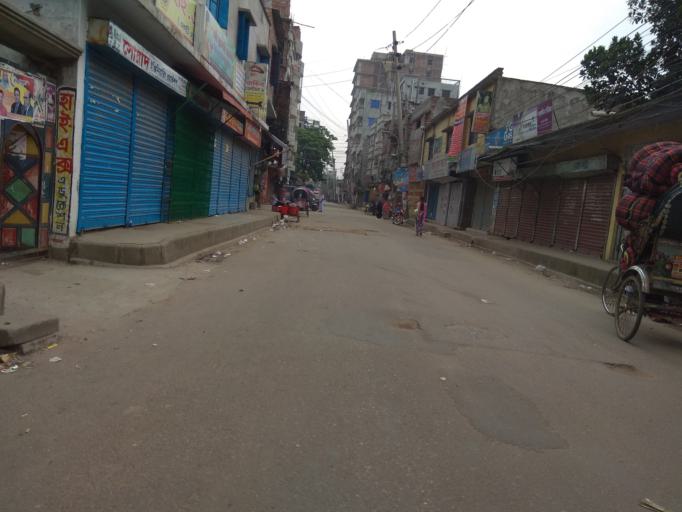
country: BD
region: Dhaka
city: Azimpur
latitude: 23.7133
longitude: 90.3713
